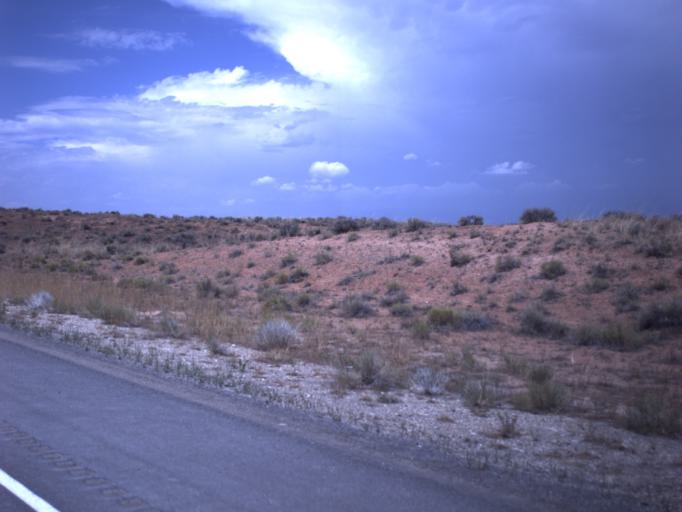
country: US
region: Utah
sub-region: Uintah County
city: Maeser
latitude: 40.3143
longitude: -109.7186
